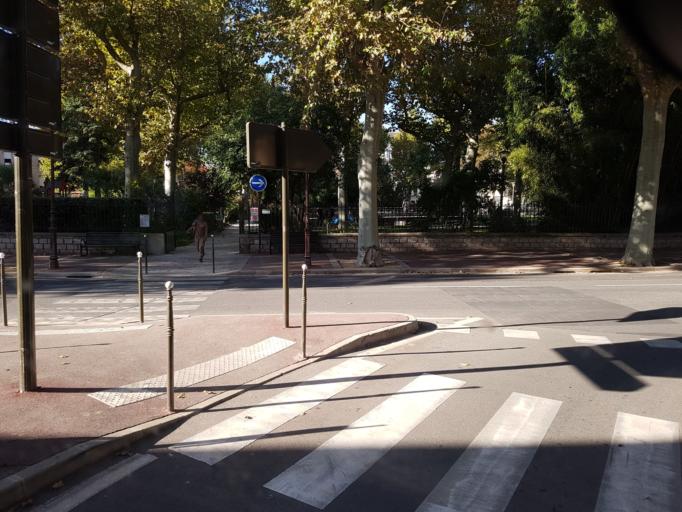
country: FR
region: Languedoc-Roussillon
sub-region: Departement de l'Aude
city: Narbonne
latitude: 43.1870
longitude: 3.0084
